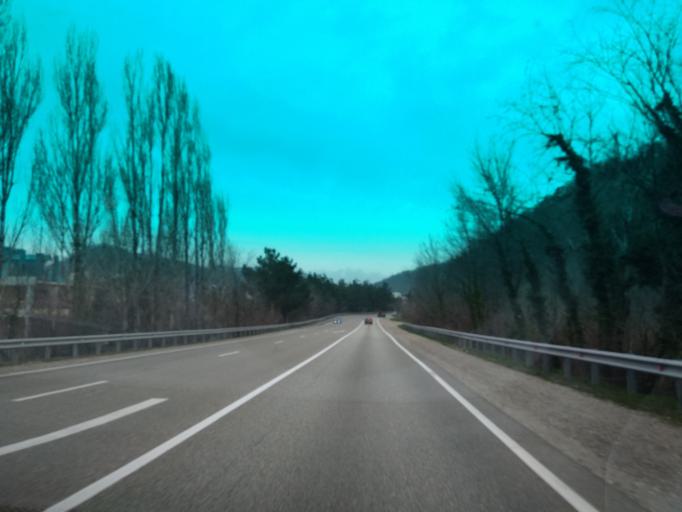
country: RU
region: Krasnodarskiy
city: Ol'ginka
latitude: 44.1916
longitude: 38.8890
